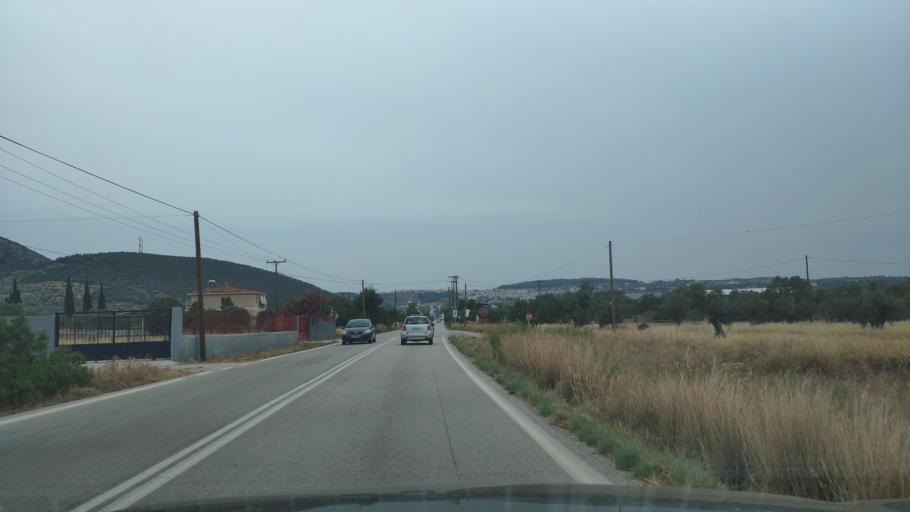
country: GR
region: Peloponnese
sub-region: Nomos Argolidos
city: Kranidi
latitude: 37.4079
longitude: 23.1541
